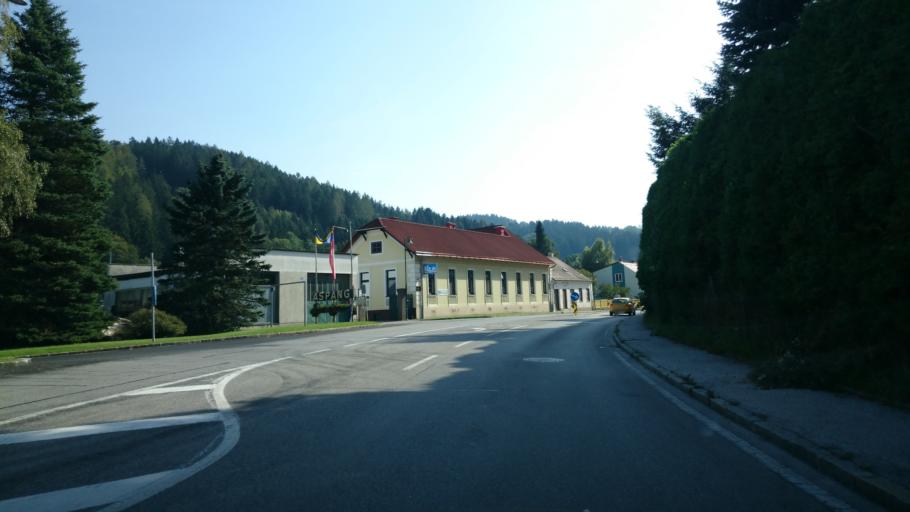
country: AT
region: Lower Austria
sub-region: Politischer Bezirk Neunkirchen
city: Thomasberg
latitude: 47.5518
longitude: 16.0870
